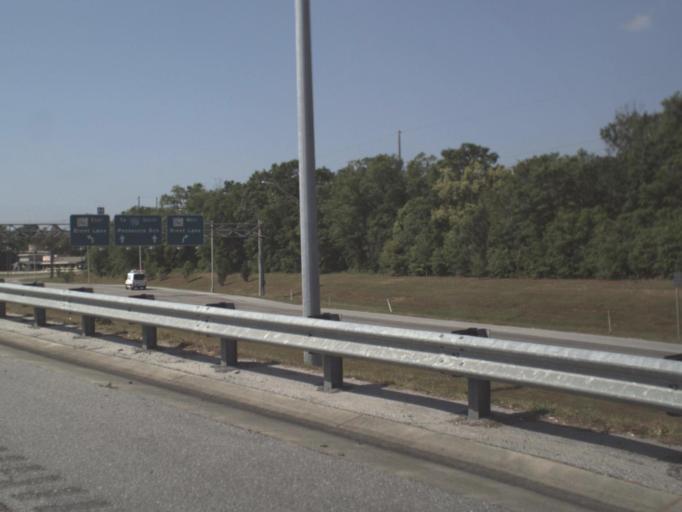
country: US
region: Florida
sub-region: Escambia County
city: Brent
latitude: 30.4744
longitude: -87.2291
